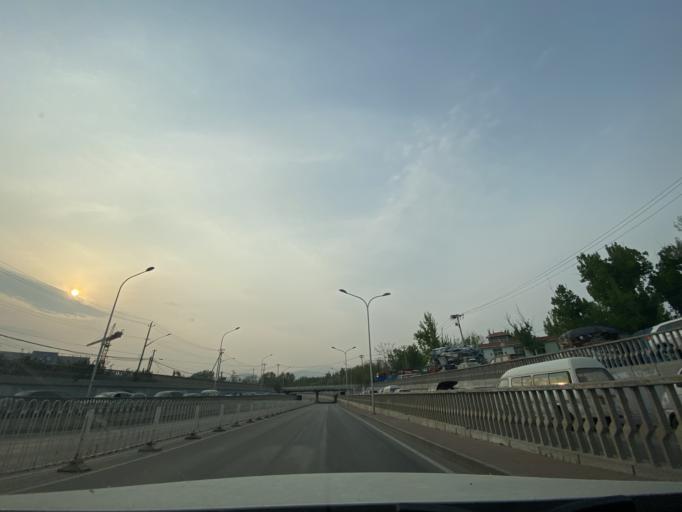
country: CN
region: Beijing
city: Babaoshan
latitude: 39.9299
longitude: 116.2291
